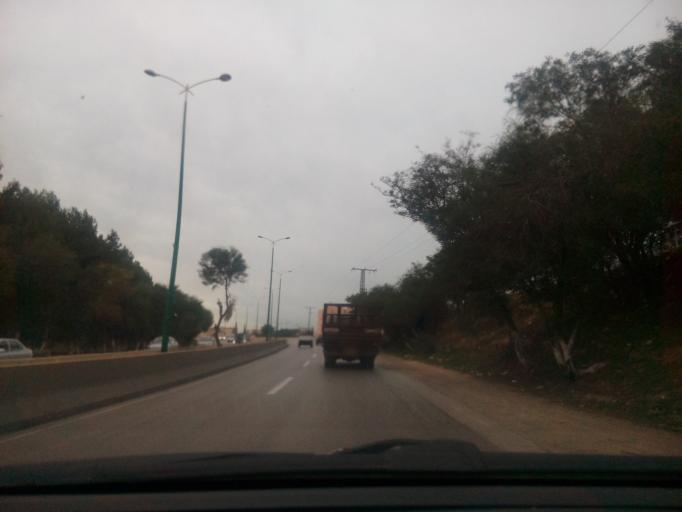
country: DZ
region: Tlemcen
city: Mansoura
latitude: 34.8992
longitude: -1.3534
